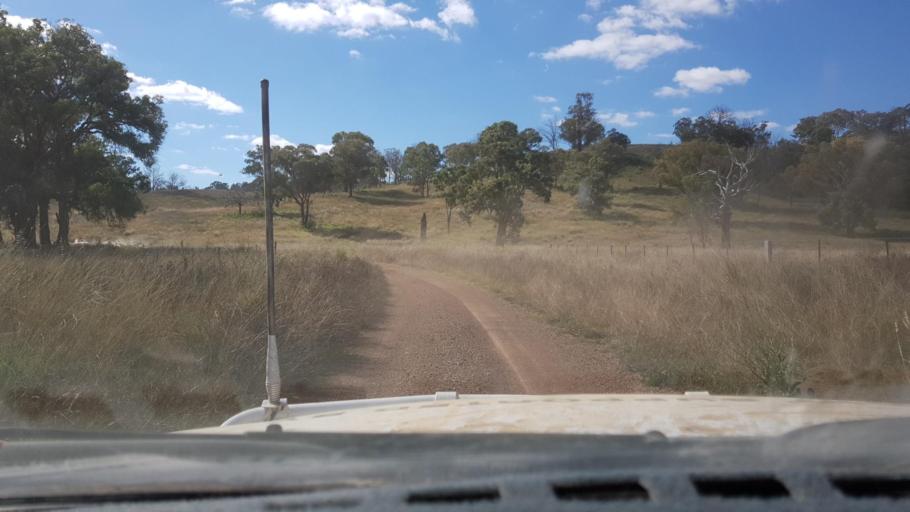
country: AU
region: New South Wales
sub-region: Tamworth Municipality
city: Manilla
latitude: -30.4410
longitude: 150.8372
